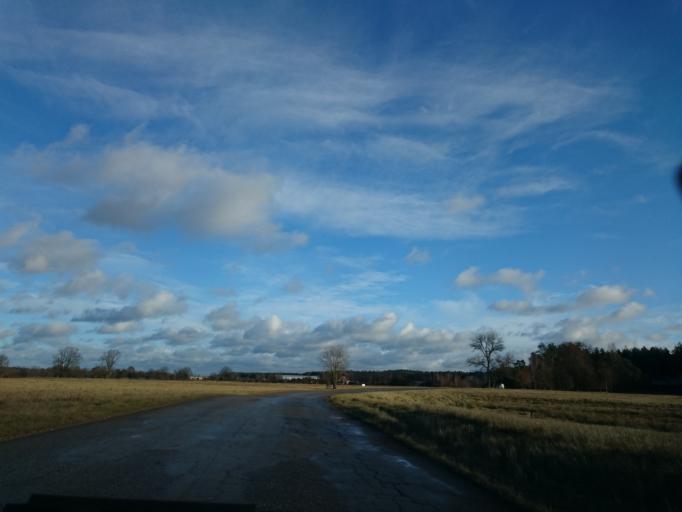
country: LV
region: Garkalne
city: Garkalne
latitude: 57.0665
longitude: 24.3956
